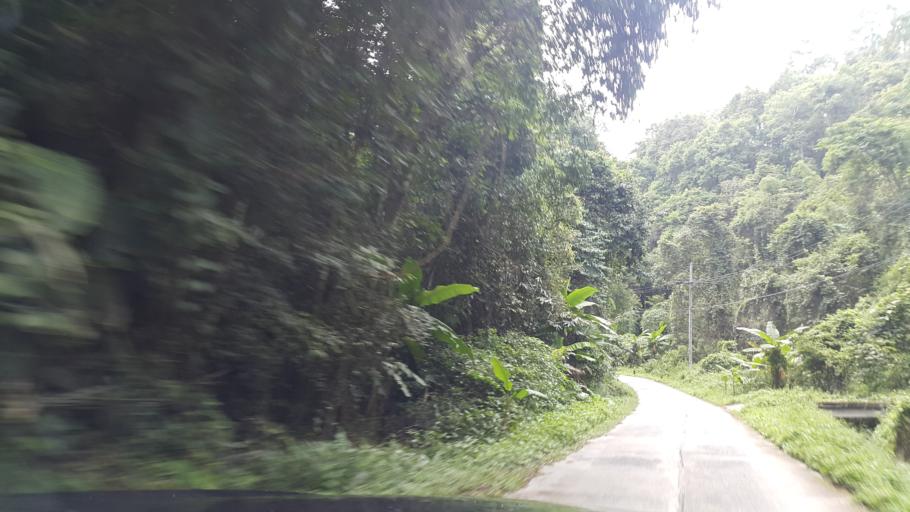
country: TH
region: Lampang
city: Wang Nuea
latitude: 19.0795
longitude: 99.3863
